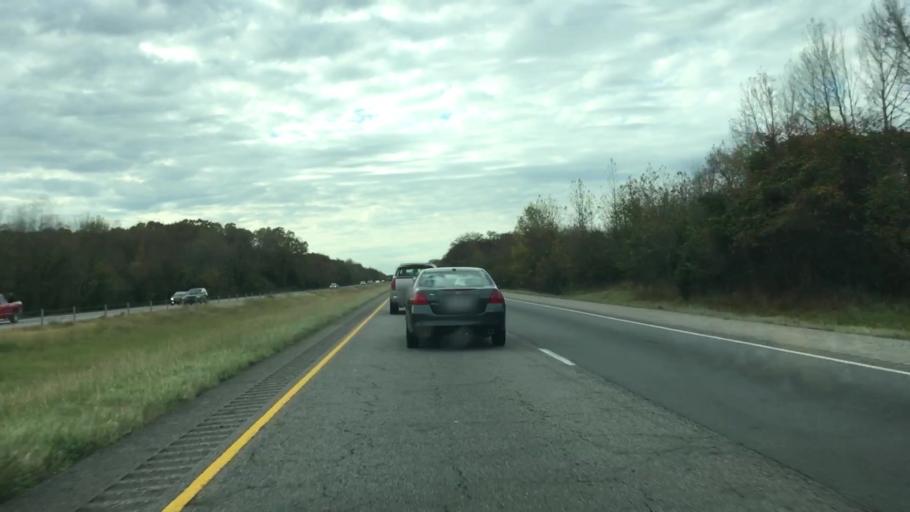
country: US
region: Arkansas
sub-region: Conway County
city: Morrilton
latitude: 35.1612
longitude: -92.5999
